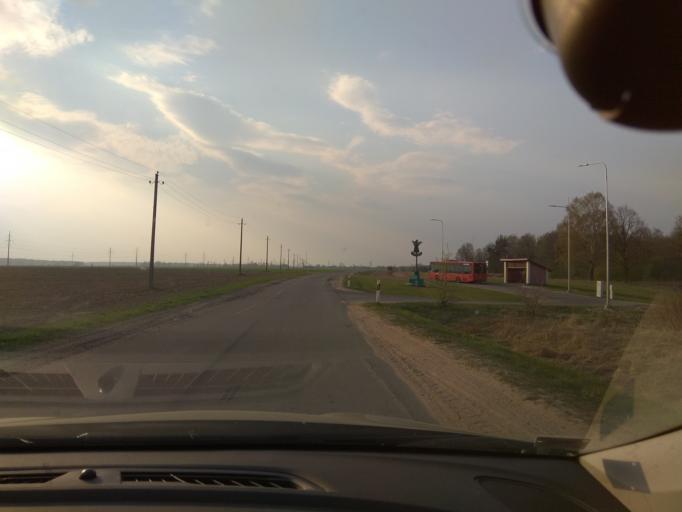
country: LT
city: Baltoji Voke
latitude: 54.6004
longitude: 25.1386
